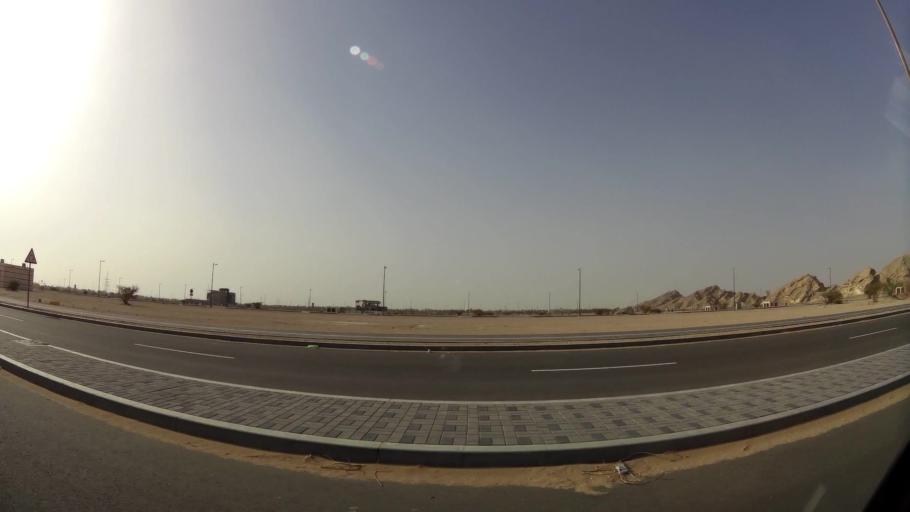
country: AE
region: Abu Dhabi
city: Al Ain
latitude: 24.1236
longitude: 55.7238
